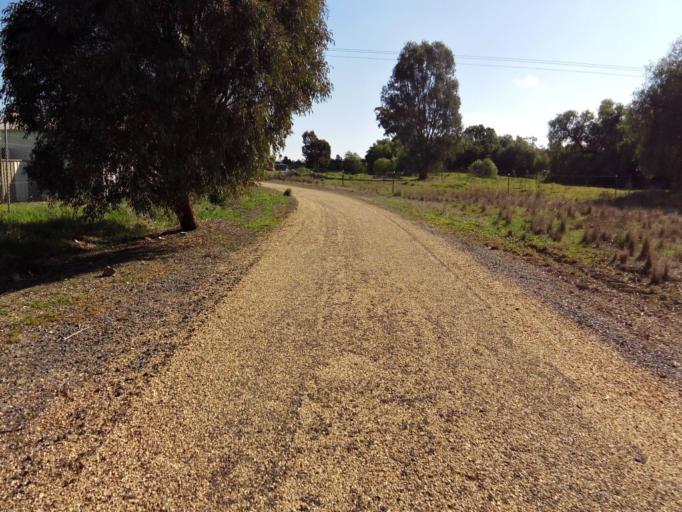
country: AU
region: New South Wales
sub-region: Corowa Shire
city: Corowa
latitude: -36.0117
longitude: 146.4037
